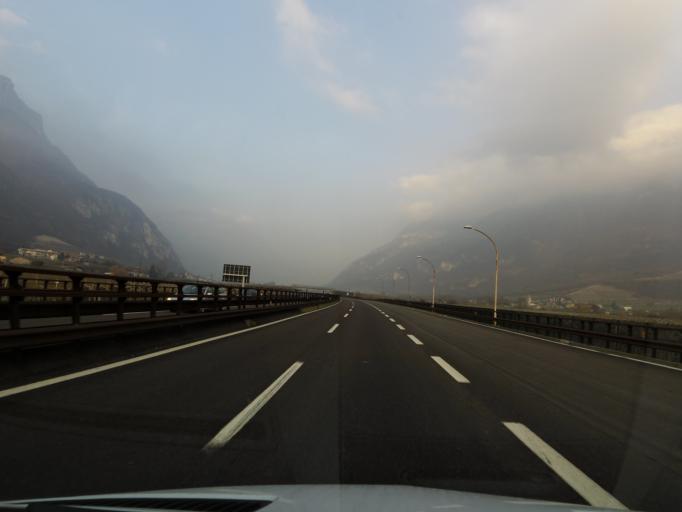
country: IT
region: Trentino-Alto Adige
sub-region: Provincia di Trento
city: Avio
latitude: 45.6963
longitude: 10.9178
